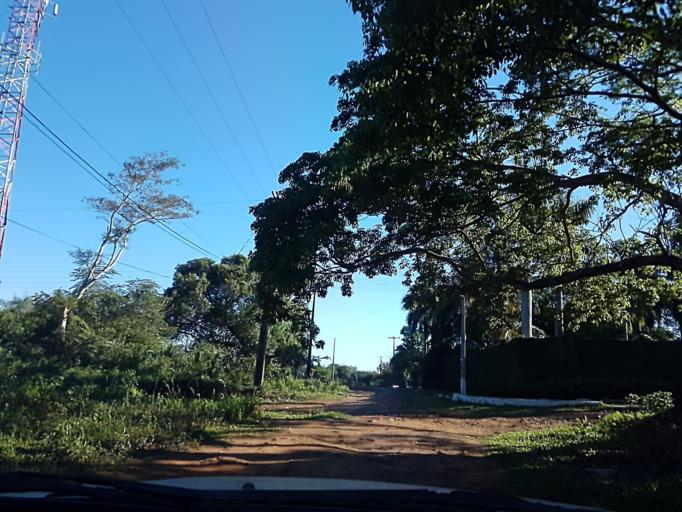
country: PY
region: Central
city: San Lorenzo
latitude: -25.2773
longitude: -57.4622
